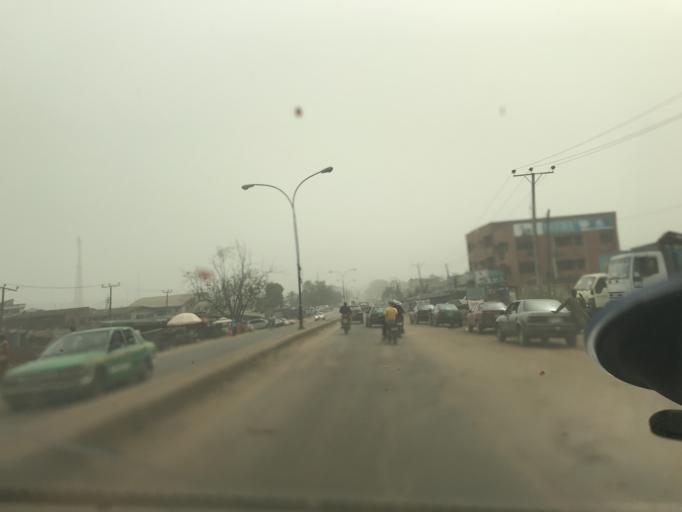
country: NG
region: Ogun
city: Shagamu
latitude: 6.8563
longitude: 3.6302
